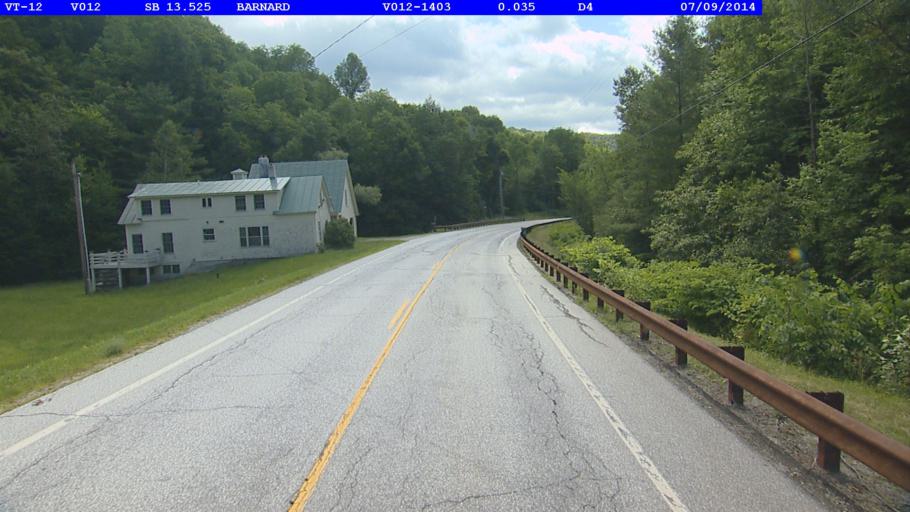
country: US
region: Vermont
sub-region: Windsor County
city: Woodstock
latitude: 43.6750
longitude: -72.5816
